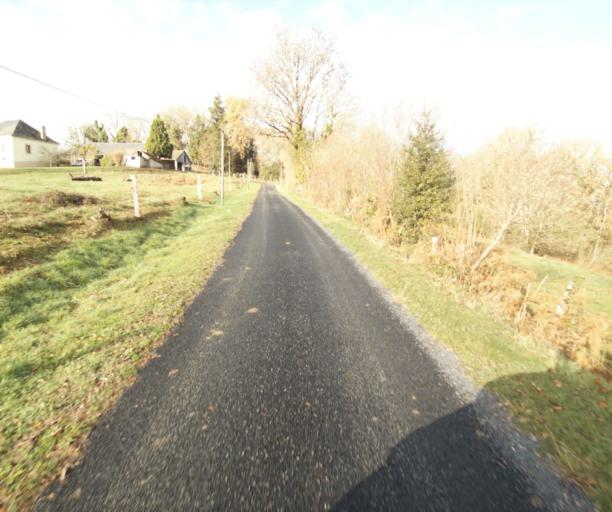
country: FR
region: Limousin
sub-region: Departement de la Correze
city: Sainte-Fereole
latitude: 45.2527
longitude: 1.6048
